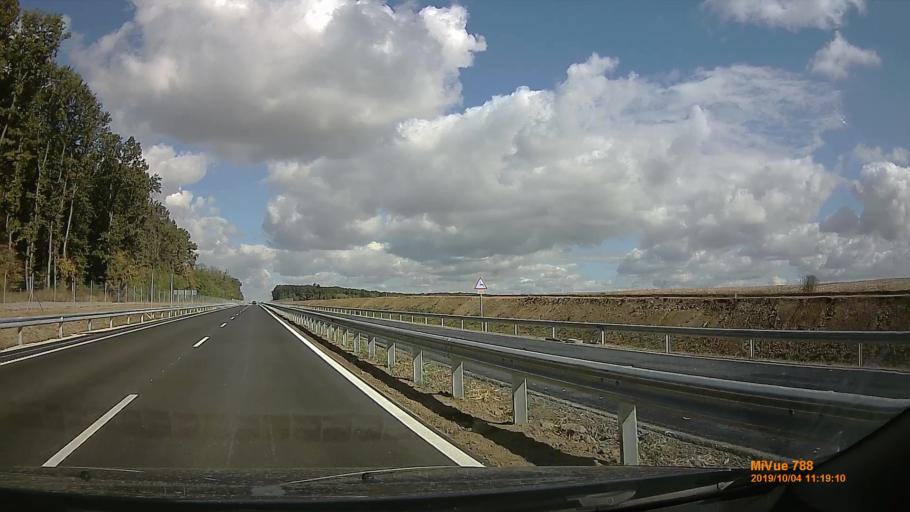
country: HU
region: Somogy
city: Kaposvar
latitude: 46.4791
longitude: 17.8045
